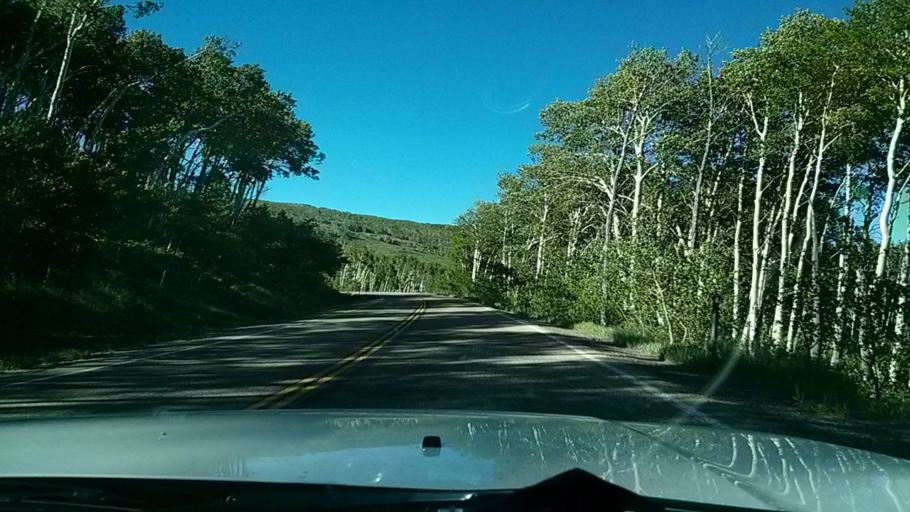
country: US
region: Utah
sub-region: Wayne County
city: Loa
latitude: 38.0194
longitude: -111.3527
